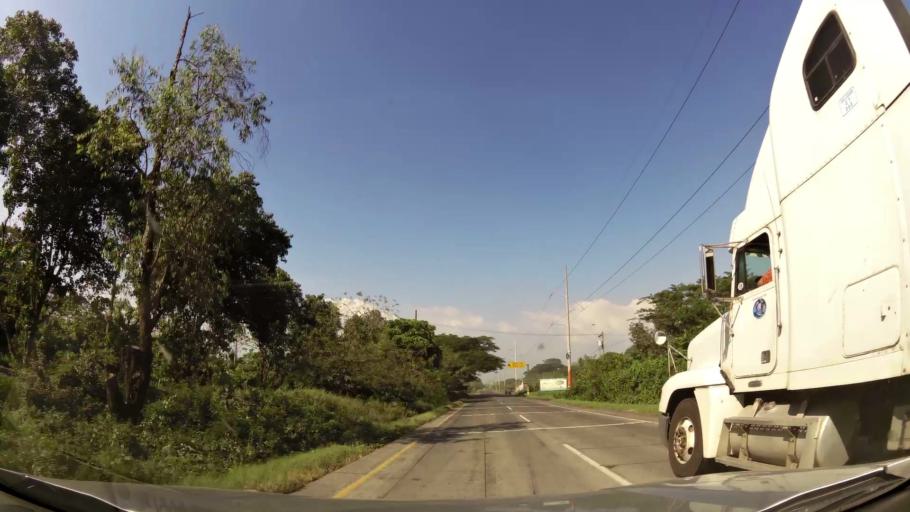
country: GT
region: Escuintla
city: Puerto San Jose
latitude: 13.9523
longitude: -90.7884
